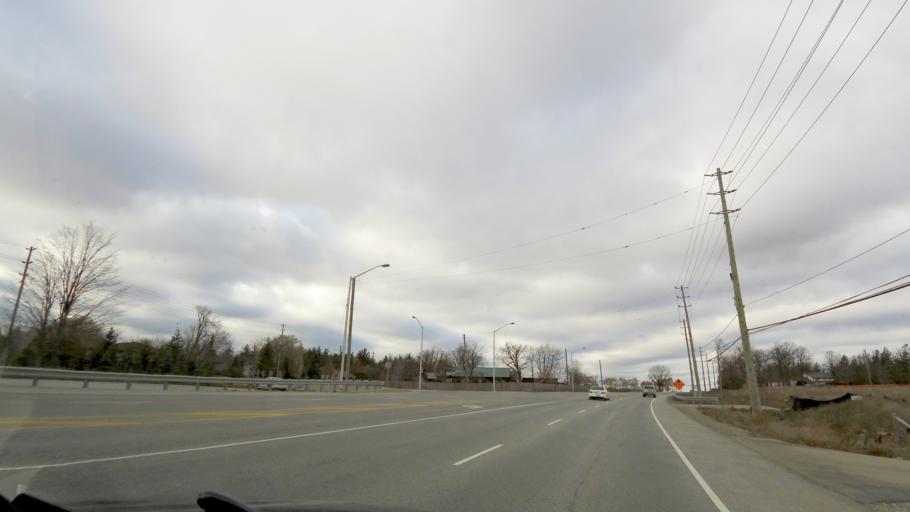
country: CA
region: Ontario
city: Burlington
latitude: 43.4550
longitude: -79.8022
